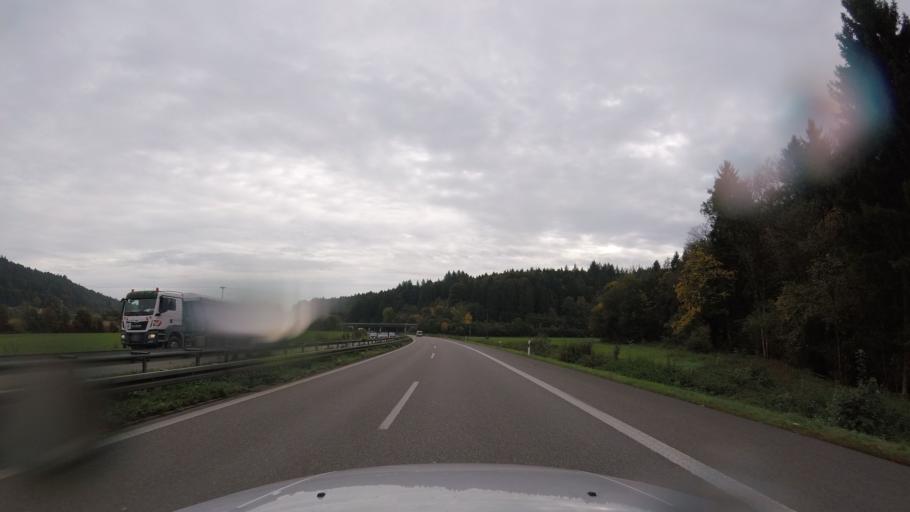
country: DE
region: Baden-Wuerttemberg
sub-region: Regierungsbezirk Stuttgart
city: Lorch
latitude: 48.7860
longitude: 9.7375
